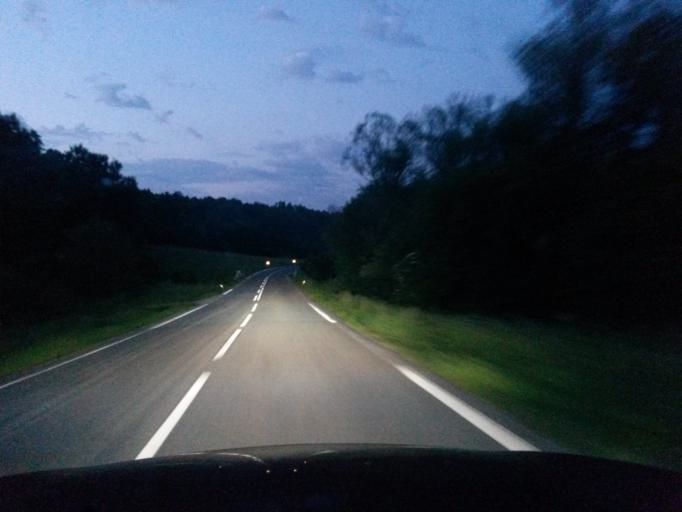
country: UA
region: Zakarpattia
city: Velykyi Bereznyi
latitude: 48.9248
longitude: 22.3270
